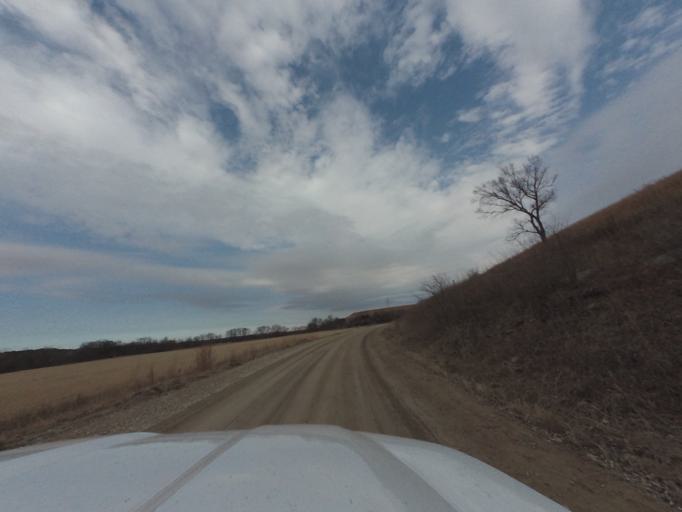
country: US
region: Kansas
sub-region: Chase County
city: Cottonwood Falls
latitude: 38.2763
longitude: -96.7337
